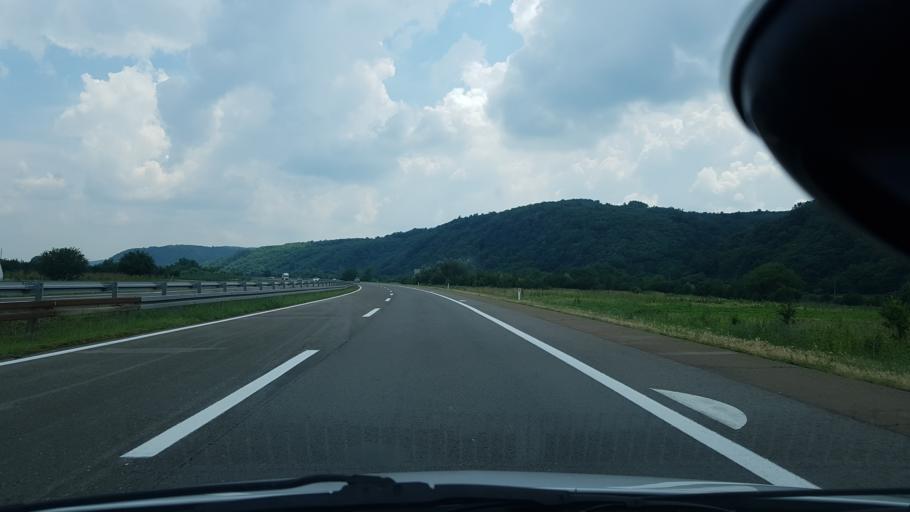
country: RS
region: Central Serbia
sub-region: Sumadijski Okrug
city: Batocina
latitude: 44.0955
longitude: 21.1671
